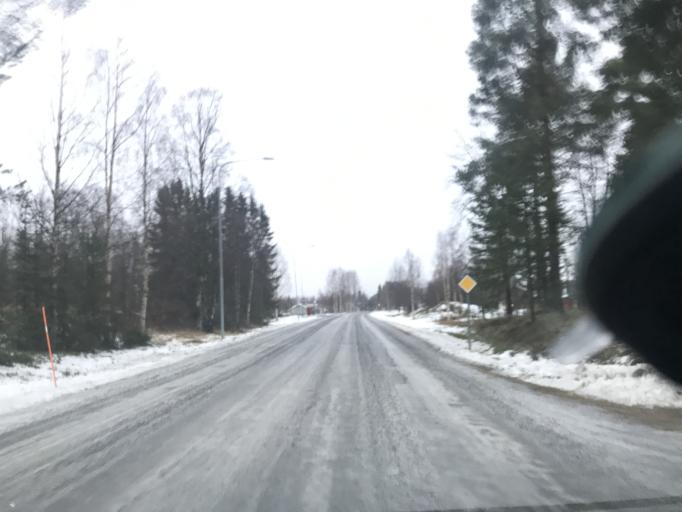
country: SE
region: Norrbotten
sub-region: Lulea Kommun
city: Sodra Sunderbyn
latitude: 65.6524
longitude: 21.9514
